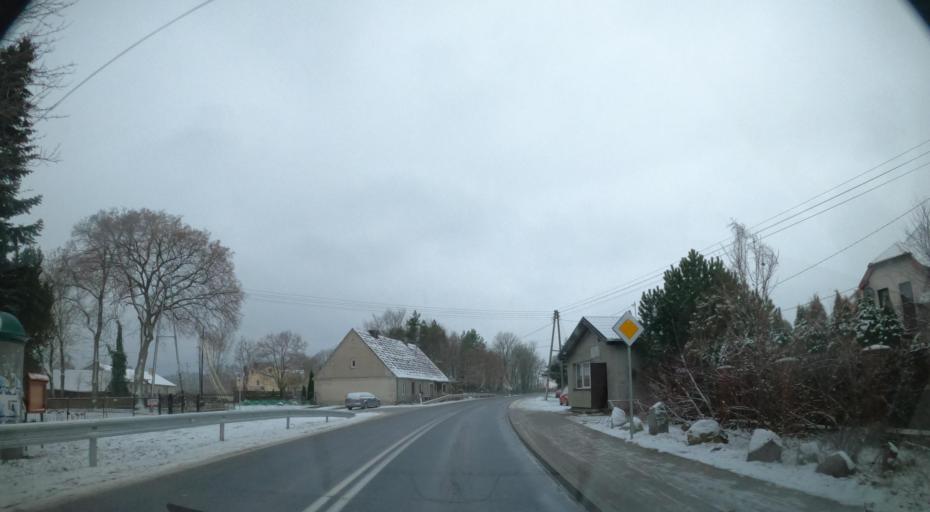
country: PL
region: Masovian Voivodeship
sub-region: Powiat plocki
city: Nowy Duninow
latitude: 52.6138
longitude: 19.4615
